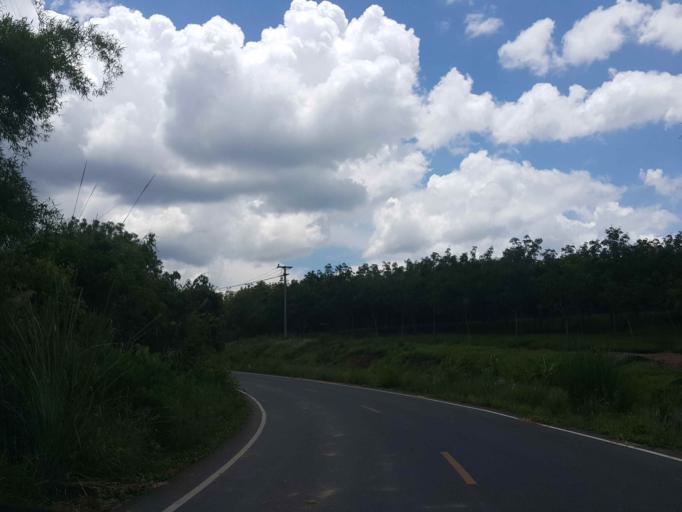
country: TH
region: Nan
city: Wiang Sa
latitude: 18.5370
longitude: 100.5491
